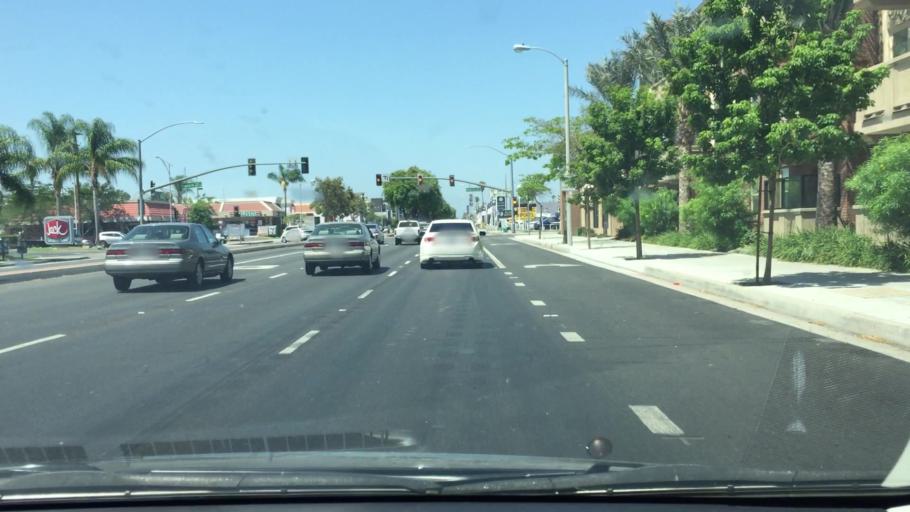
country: US
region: California
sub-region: Orange County
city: Garden Grove
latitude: 33.7517
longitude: -117.9201
